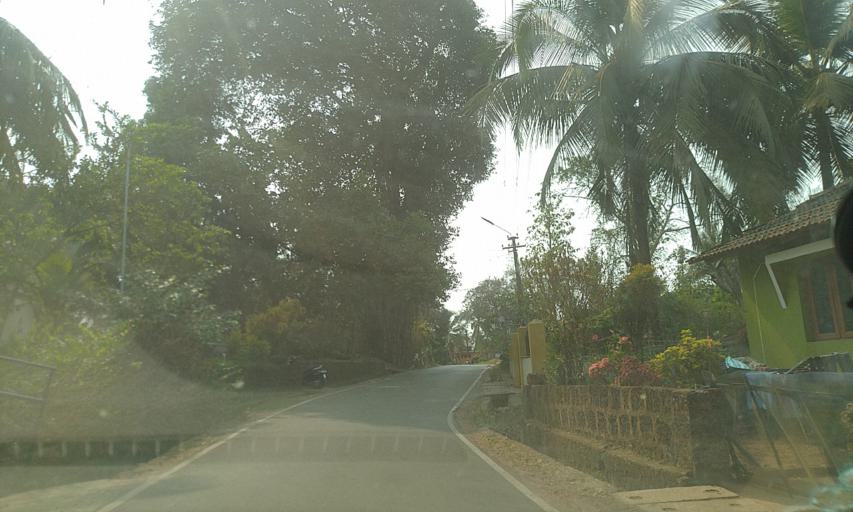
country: IN
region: Goa
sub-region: South Goa
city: Quepem
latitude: 15.2538
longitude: 74.0468
